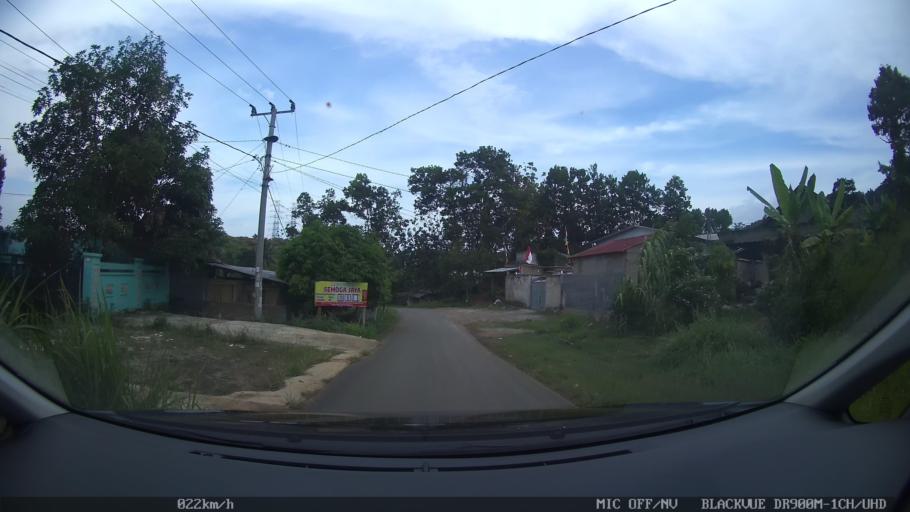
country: ID
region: Lampung
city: Bandarlampung
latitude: -5.4051
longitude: 105.1921
